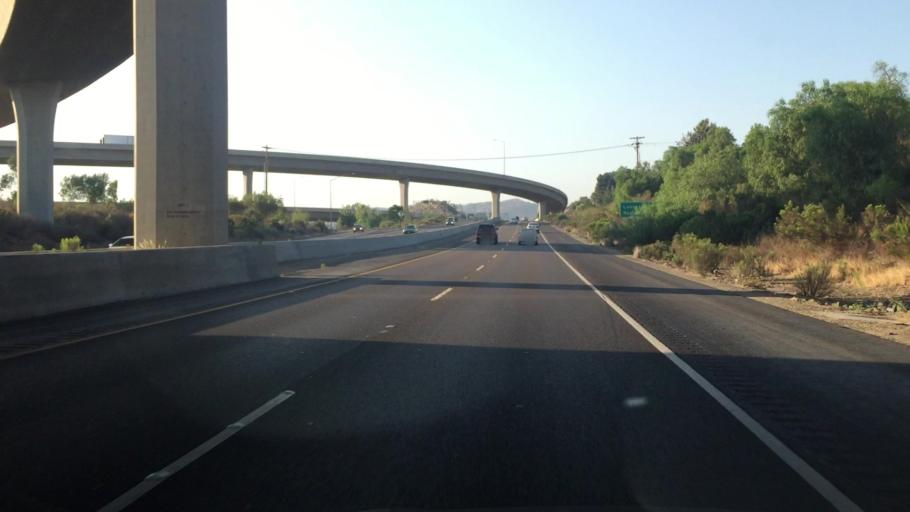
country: US
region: California
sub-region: San Diego County
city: Santee
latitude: 32.8311
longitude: -116.9618
